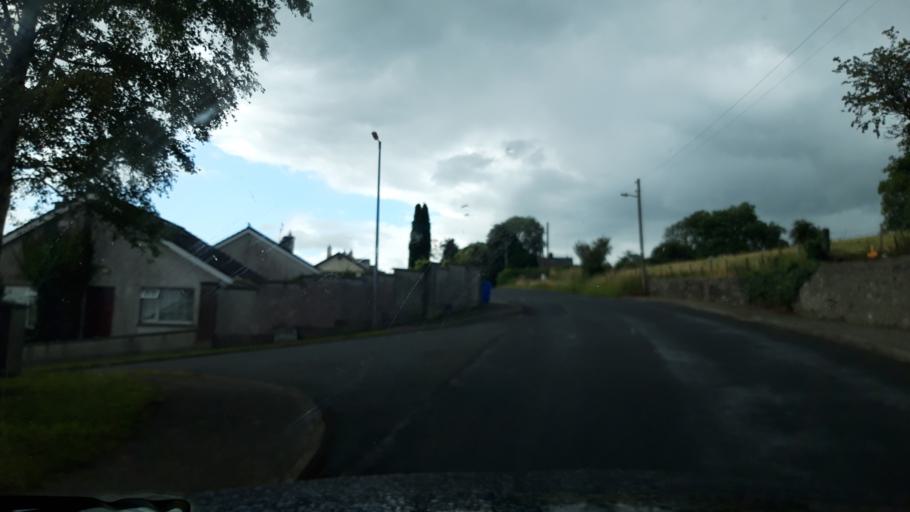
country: IE
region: Leinster
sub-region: Wicklow
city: Baltinglass
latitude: 52.9427
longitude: -6.7052
